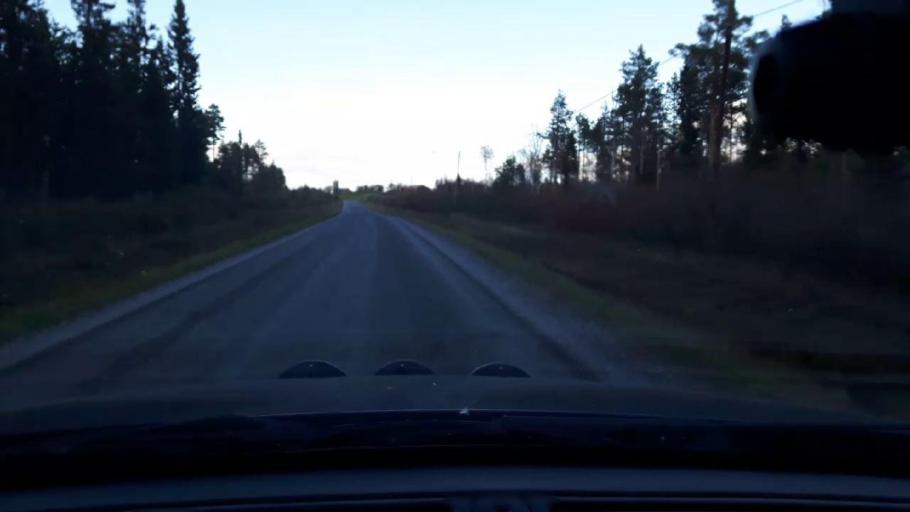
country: SE
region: Jaemtland
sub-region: Krokoms Kommun
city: Krokom
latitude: 63.0737
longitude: 14.2704
